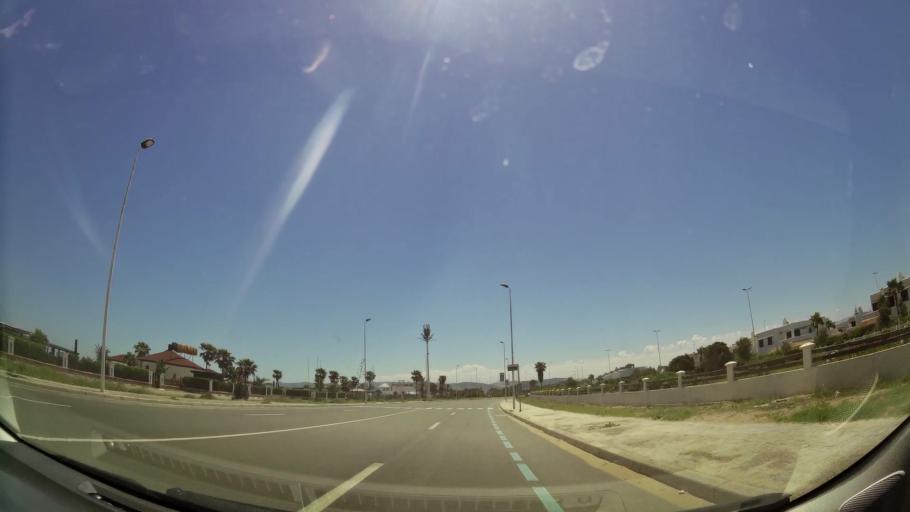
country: MA
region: Oriental
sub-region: Berkane-Taourirt
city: Madagh
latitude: 35.0969
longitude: -2.2636
